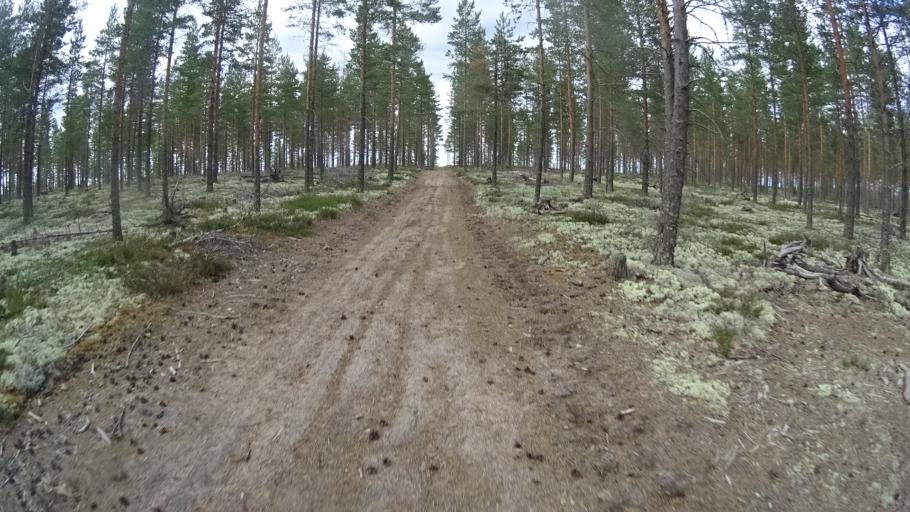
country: FI
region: Satakunta
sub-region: Pohjois-Satakunta
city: Jaemijaervi
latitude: 61.7707
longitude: 22.8042
